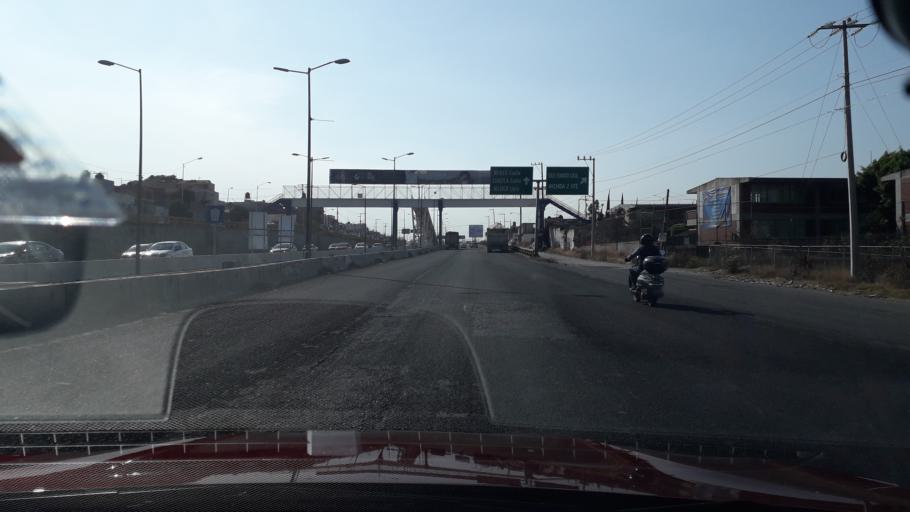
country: MX
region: Puebla
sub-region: Puebla
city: El Capulo (La Quebradora)
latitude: 18.9816
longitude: -98.2253
